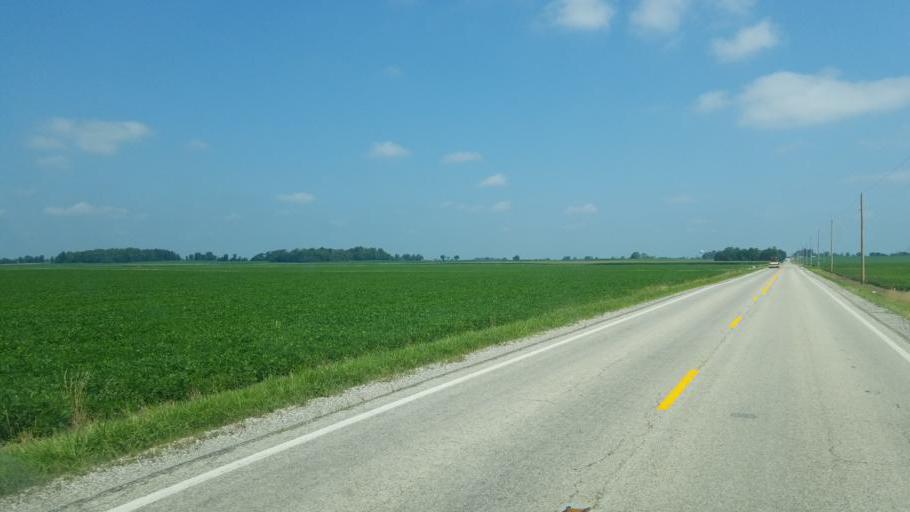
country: US
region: Ohio
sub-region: Huron County
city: Willard
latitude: 40.9346
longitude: -82.8541
